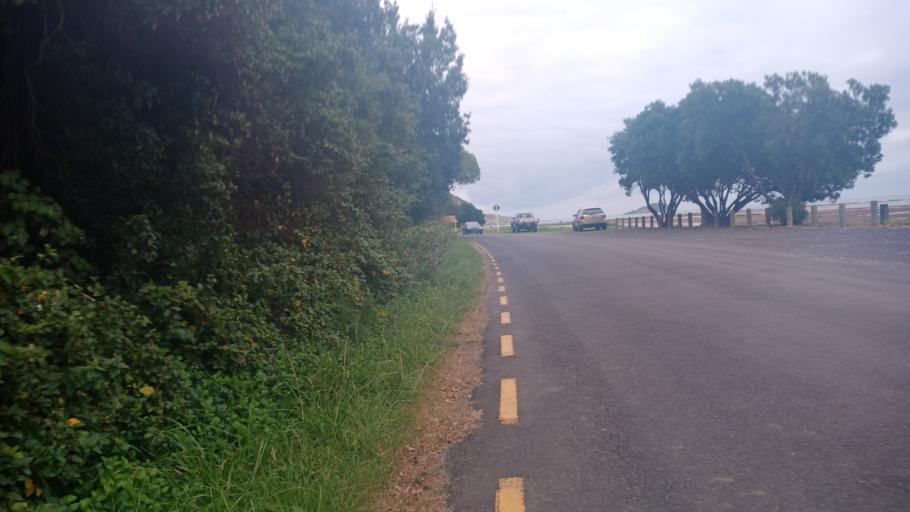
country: NZ
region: Gisborne
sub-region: Gisborne District
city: Gisborne
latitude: -38.6803
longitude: 178.0276
